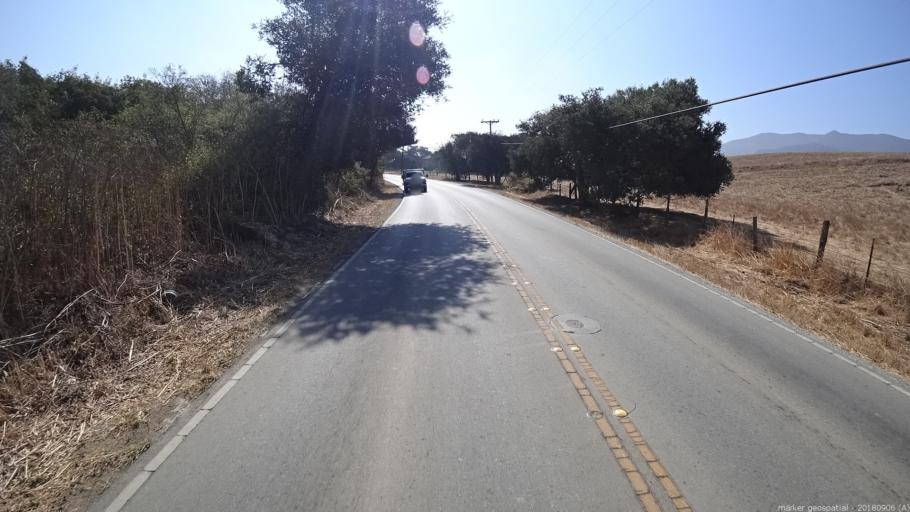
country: US
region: California
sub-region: Monterey County
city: Chualar
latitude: 36.5635
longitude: -121.5634
